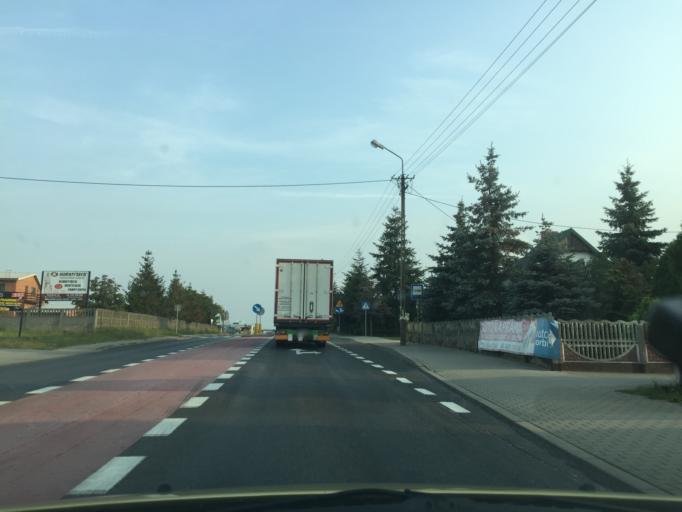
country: PL
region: Greater Poland Voivodeship
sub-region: Powiat jarocinski
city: Jarocin
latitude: 52.0071
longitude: 17.4734
